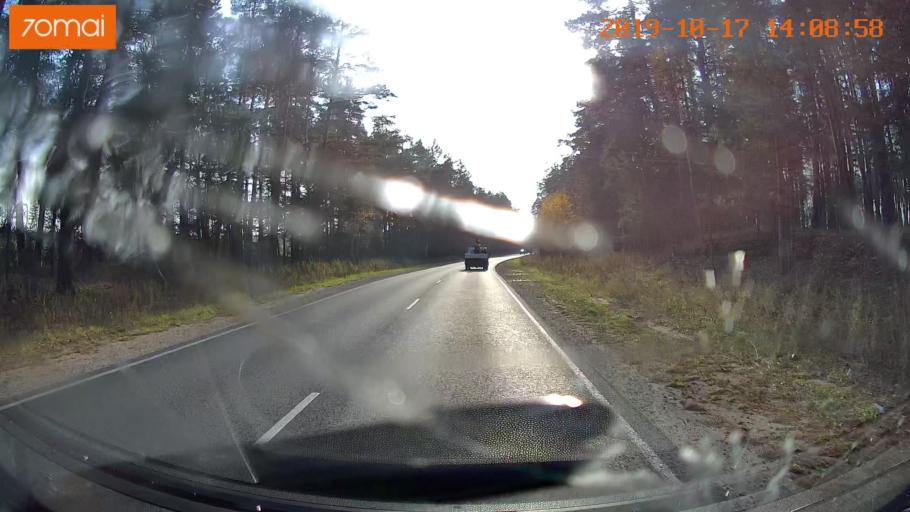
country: RU
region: Rjazan
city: Spas-Klepiki
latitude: 55.0940
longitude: 40.0635
